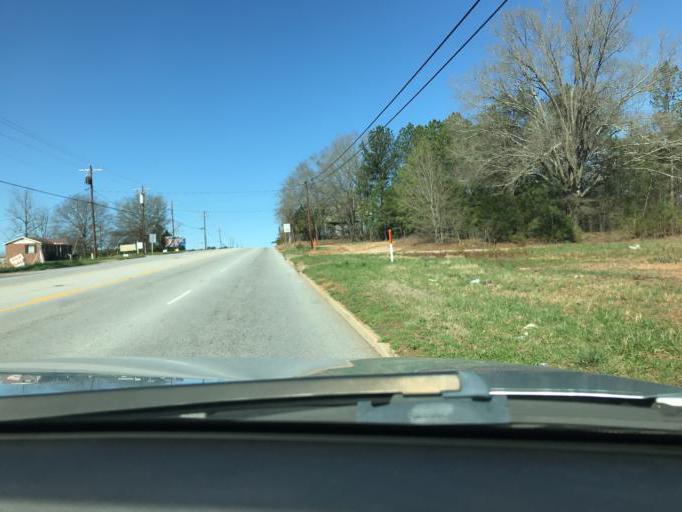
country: US
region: South Carolina
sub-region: Laurens County
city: Watts Mills
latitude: 34.4907
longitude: -81.9718
